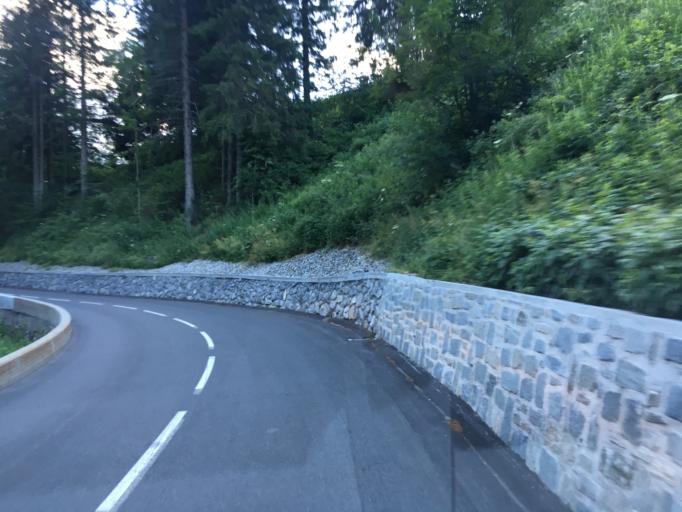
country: CH
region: Valais
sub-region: Saint-Maurice District
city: Salvan
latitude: 46.0396
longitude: 6.9378
